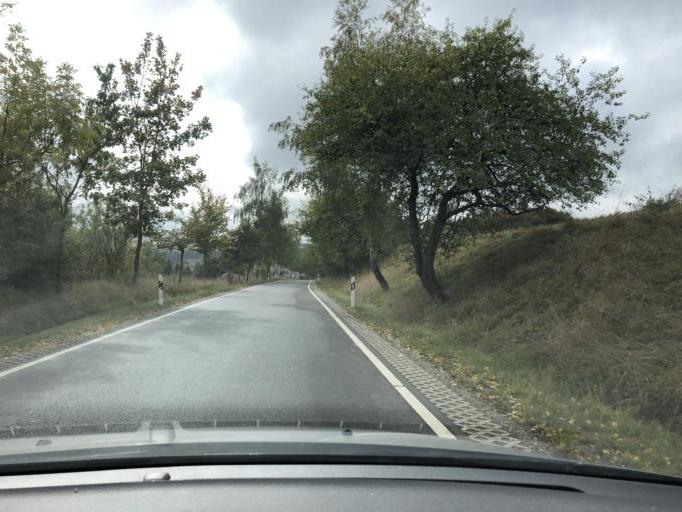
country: DE
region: Thuringia
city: Kreuzebra
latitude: 51.3487
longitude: 10.2602
